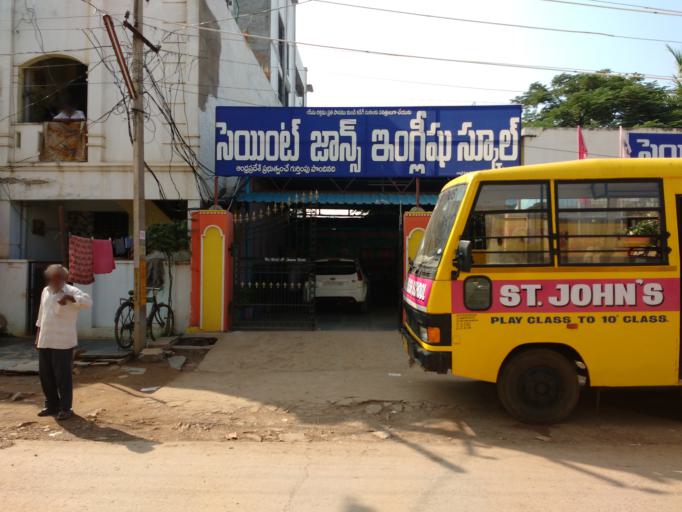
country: IN
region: Andhra Pradesh
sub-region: Kurnool
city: Nandyal
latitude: 15.4847
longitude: 78.4798
